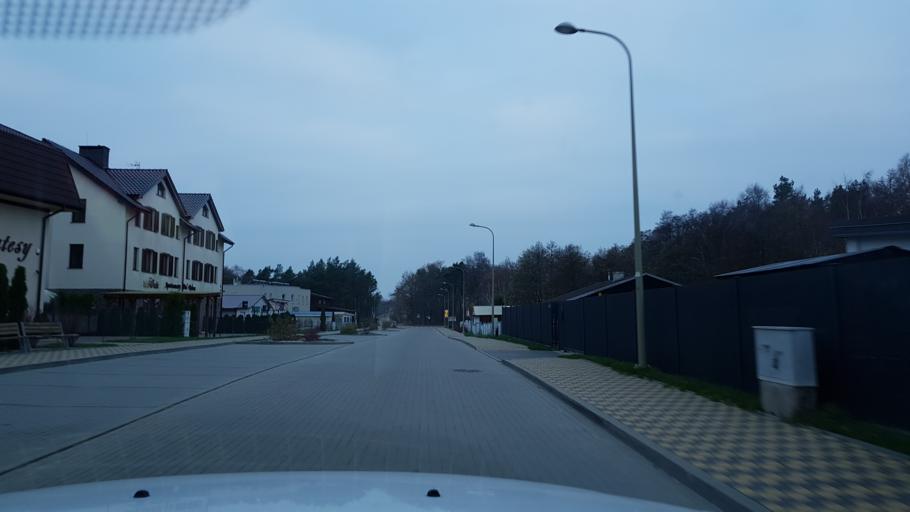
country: PL
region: West Pomeranian Voivodeship
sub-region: Powiat slawienski
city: Darlowo
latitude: 54.5067
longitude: 16.4688
